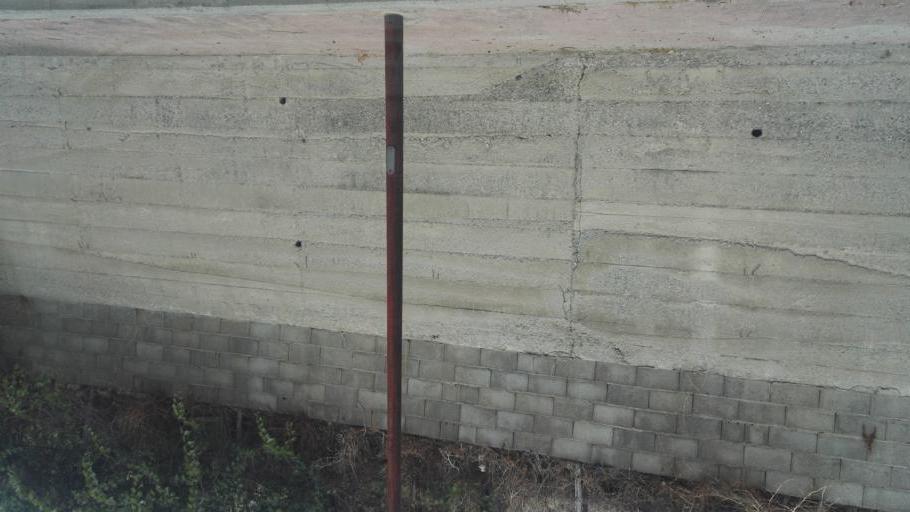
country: IT
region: Calabria
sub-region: Provincia di Reggio Calabria
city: Roccella Ionica
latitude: 38.3261
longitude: 16.4107
